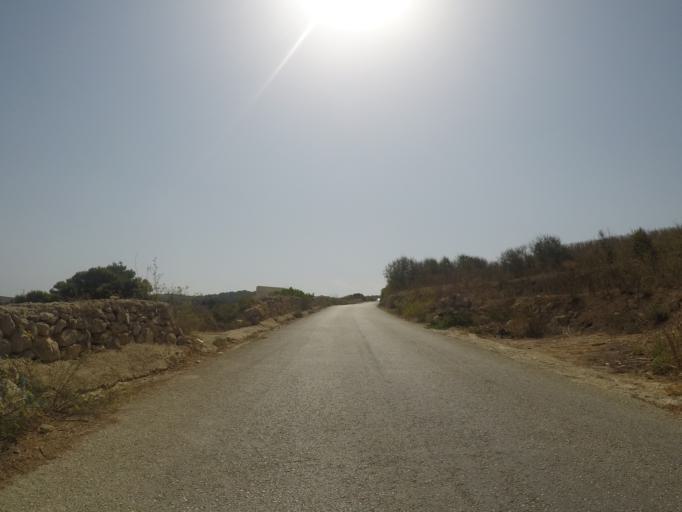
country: MT
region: L-Imgarr
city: Imgarr
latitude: 35.9393
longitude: 14.3761
